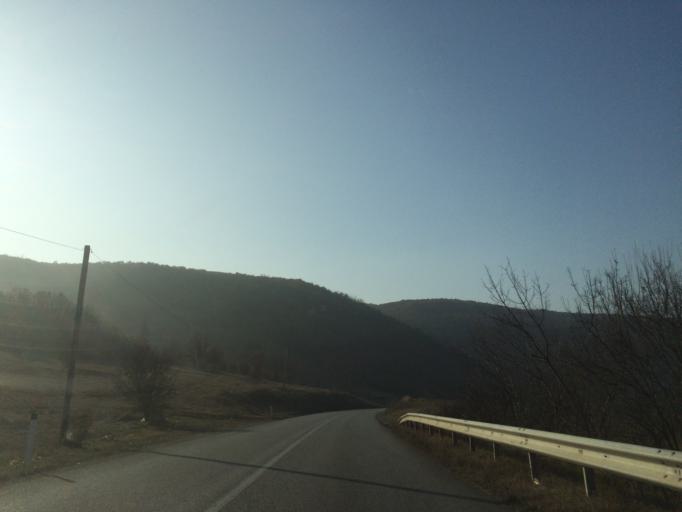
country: XK
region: Pec
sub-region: Komuna e Pejes
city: Kosuriq
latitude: 42.5101
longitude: 20.5464
